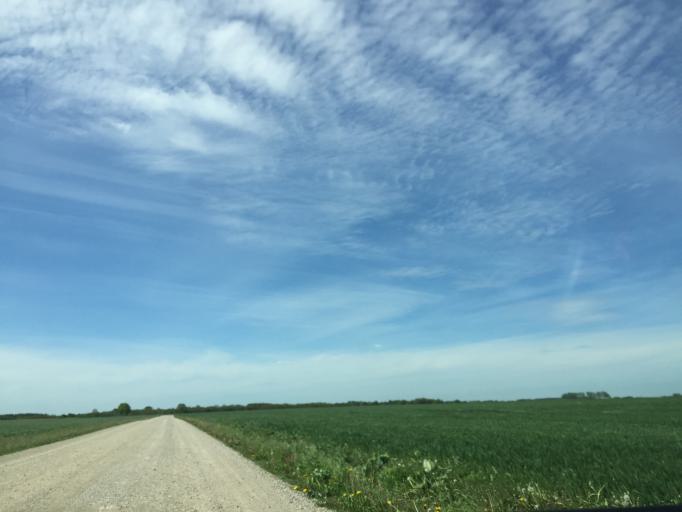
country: LT
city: Linkuva
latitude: 56.0843
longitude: 24.1172
